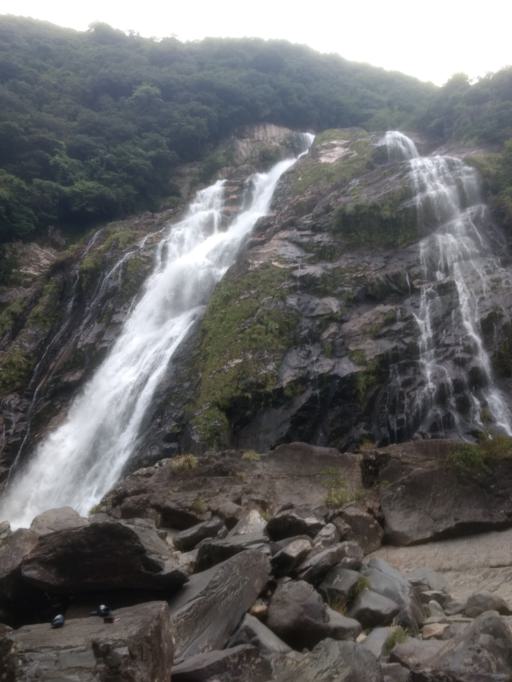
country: JP
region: Kagoshima
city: Nishinoomote
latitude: 30.2995
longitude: 130.4137
